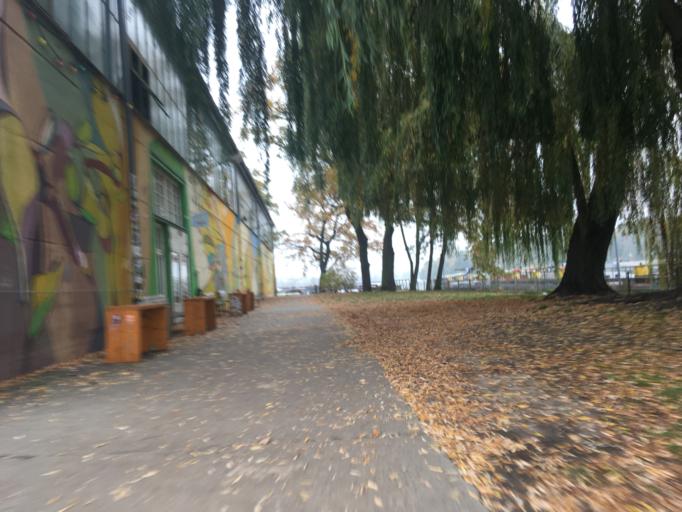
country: DE
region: Berlin
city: Rummelsburg
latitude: 52.4916
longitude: 13.4877
